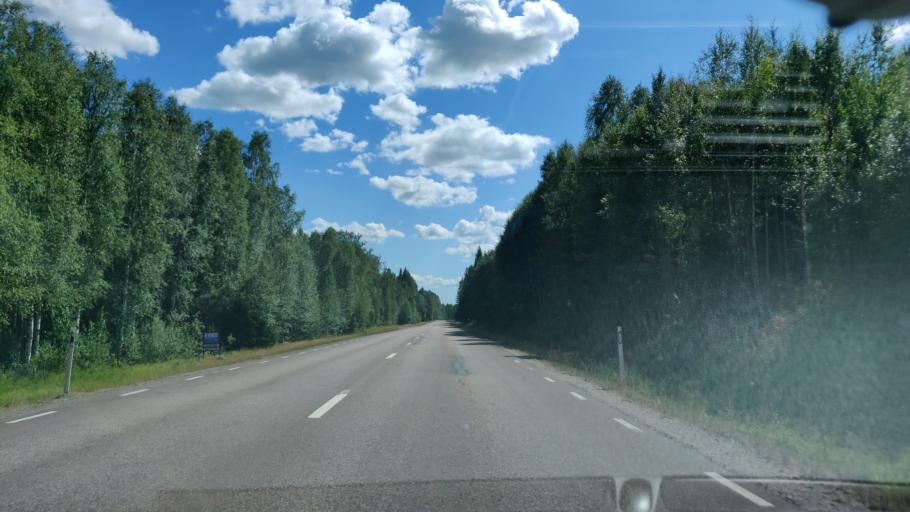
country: SE
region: Vaermland
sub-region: Hagfors Kommun
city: Ekshaerad
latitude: 60.2018
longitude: 13.4933
